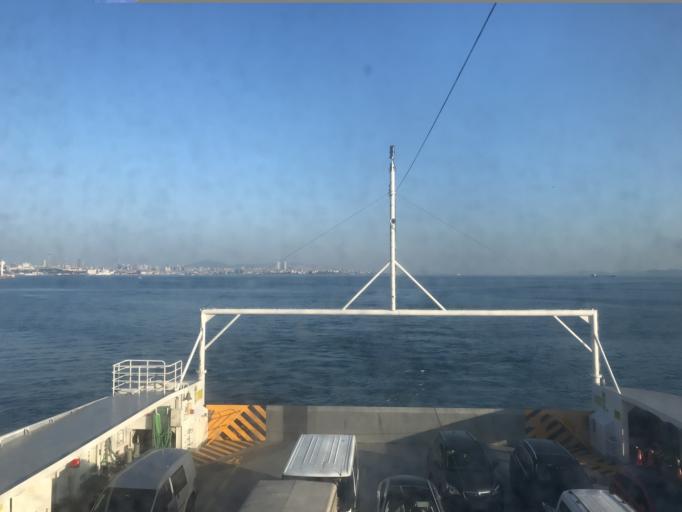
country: TR
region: Istanbul
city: Istanbul
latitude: 40.9995
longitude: 28.9610
